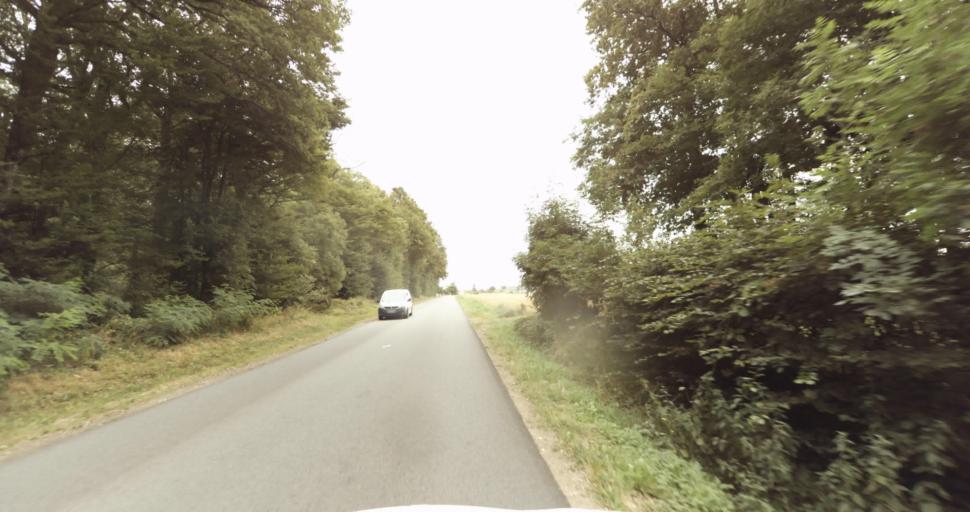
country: FR
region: Haute-Normandie
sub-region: Departement de l'Eure
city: Arnieres-sur-Iton
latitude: 48.9649
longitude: 1.1128
